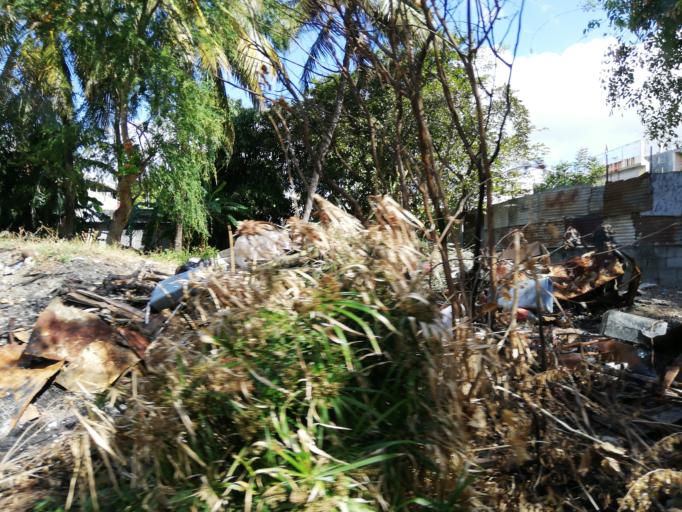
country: MU
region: Port Louis
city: Port Louis
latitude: -20.1602
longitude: 57.4821
